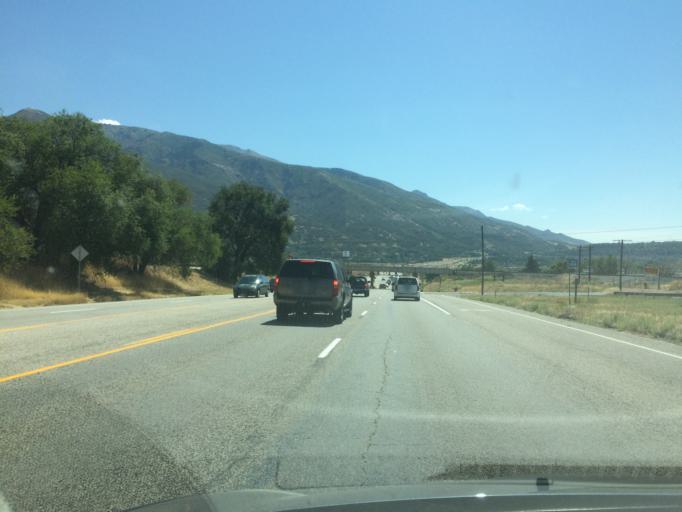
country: US
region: Utah
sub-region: Weber County
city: Uintah
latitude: 41.1429
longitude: -111.9177
